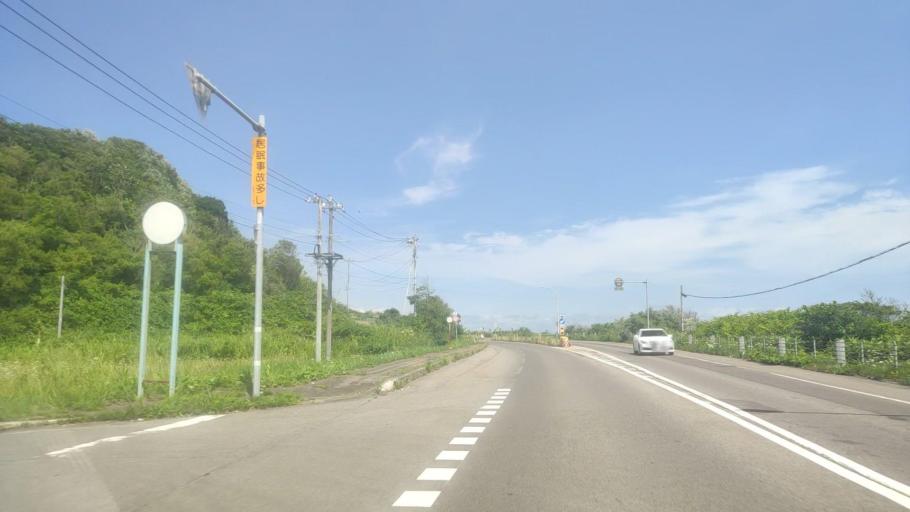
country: JP
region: Hokkaido
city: Nanae
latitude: 42.1959
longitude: 140.4199
